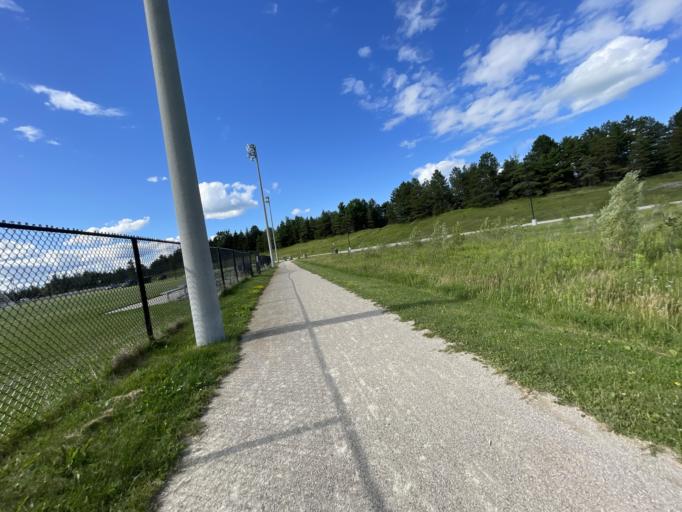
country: CA
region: Ontario
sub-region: Wellington County
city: Guelph
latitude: 43.5804
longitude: -80.2302
